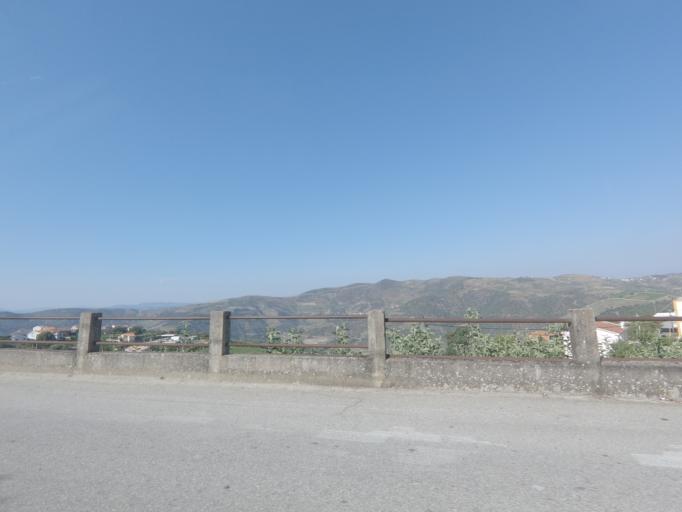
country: PT
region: Viseu
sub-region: Tabuaco
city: Tabuaco
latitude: 41.1153
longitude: -7.5626
